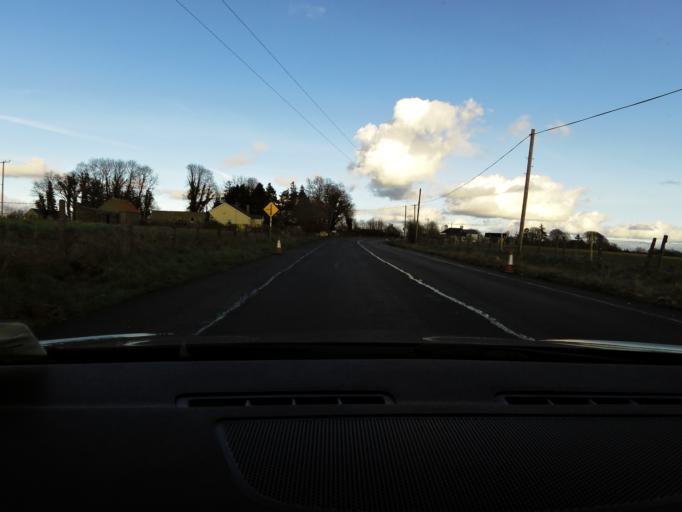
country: IE
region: Connaught
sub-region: Roscommon
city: Castlerea
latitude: 53.6893
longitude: -8.4077
